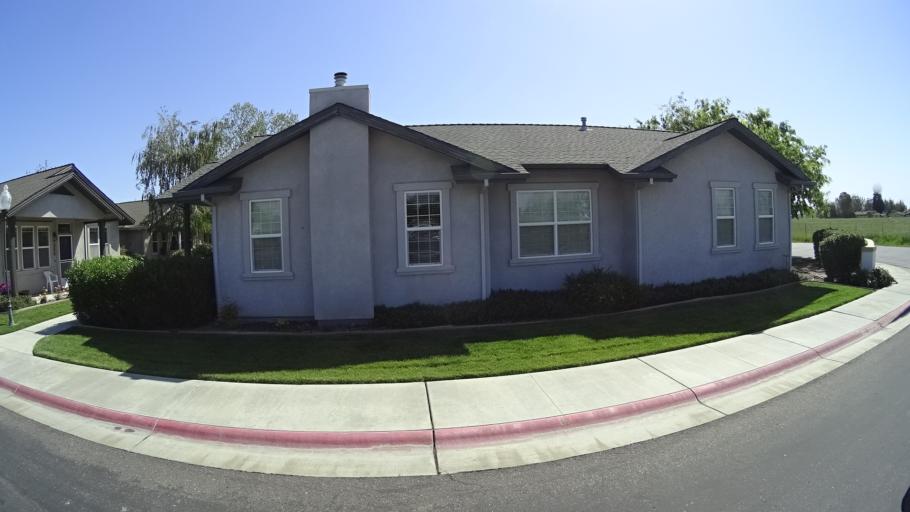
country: US
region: California
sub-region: Glenn County
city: Orland
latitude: 39.7368
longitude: -122.1850
